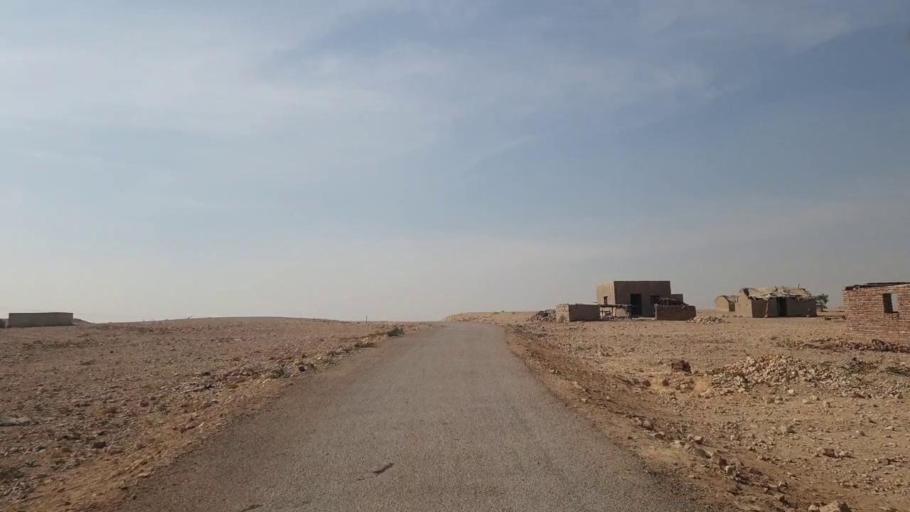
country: PK
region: Sindh
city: Hala
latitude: 25.7800
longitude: 68.2795
